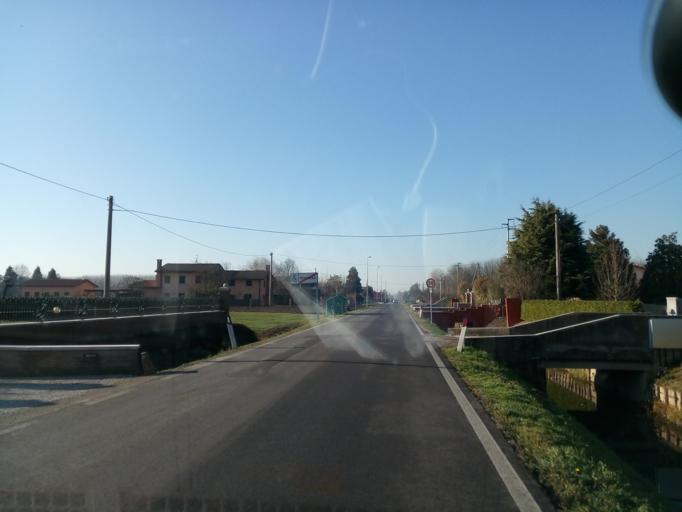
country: IT
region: Veneto
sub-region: Provincia di Venezia
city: Veternigo
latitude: 45.5150
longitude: 12.0513
